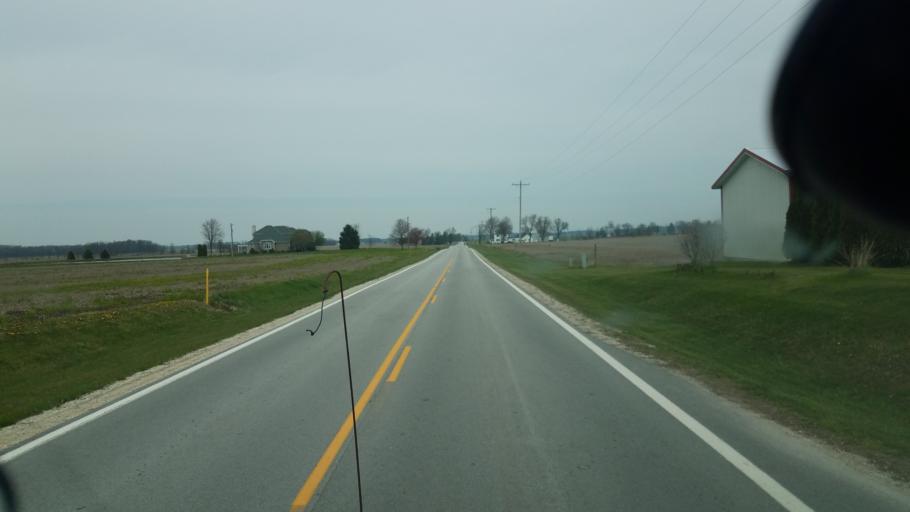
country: US
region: Ohio
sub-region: Wyandot County
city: Carey
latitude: 40.9772
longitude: -83.4767
